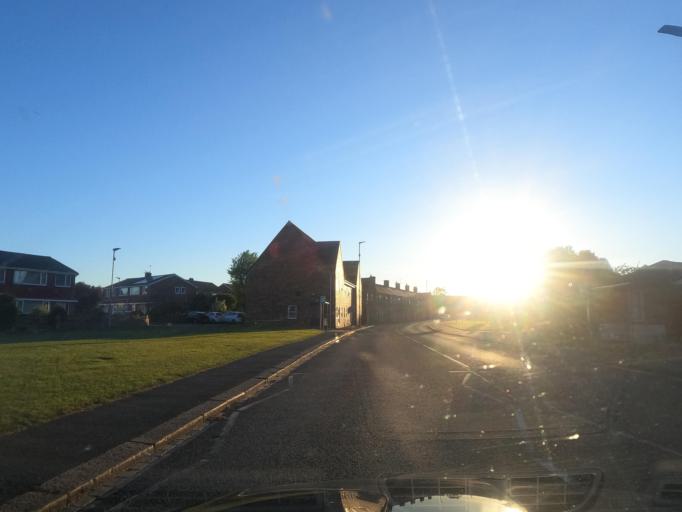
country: GB
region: England
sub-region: Northumberland
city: Blyth
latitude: 55.1274
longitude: -1.5187
